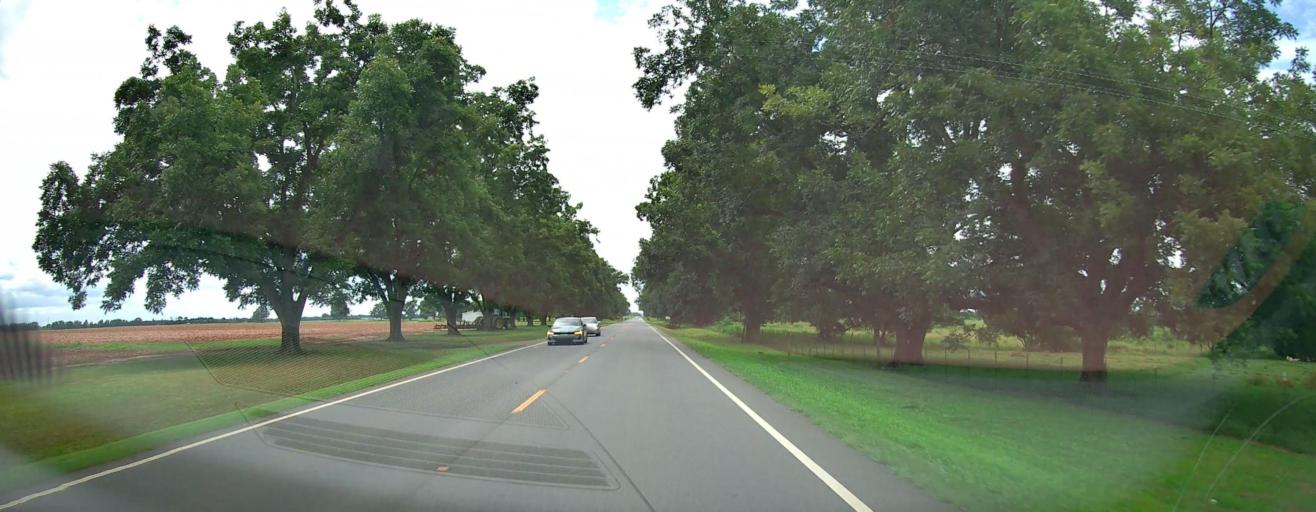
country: US
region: Georgia
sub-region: Macon County
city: Montezuma
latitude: 32.2931
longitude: -83.9648
